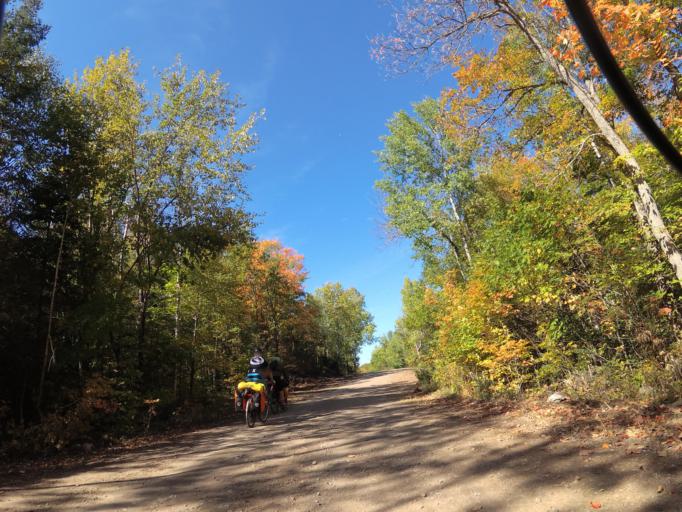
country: CA
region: Ontario
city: Renfrew
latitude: 45.3348
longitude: -77.0587
